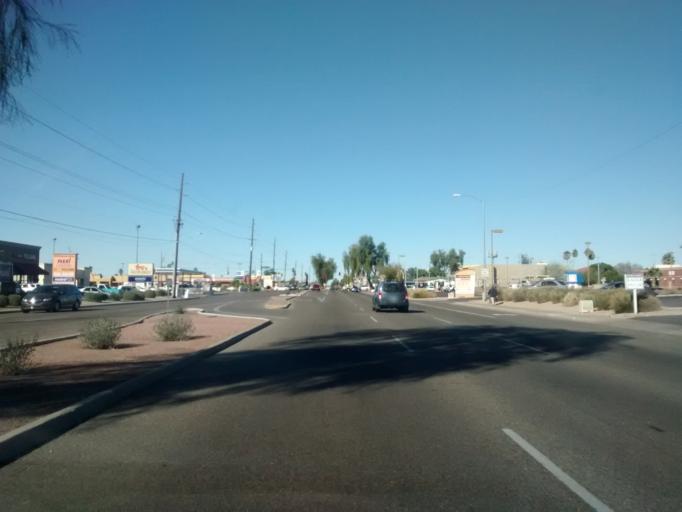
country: US
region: Arizona
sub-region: Maricopa County
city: Glendale
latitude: 33.5801
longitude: -112.1341
